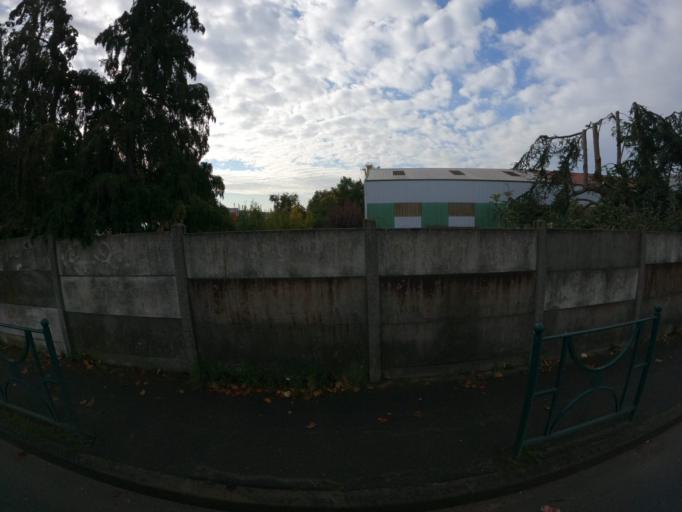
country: FR
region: Ile-de-France
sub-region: Departement de Seine-et-Marne
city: Courtry
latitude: 48.9112
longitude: 2.6047
